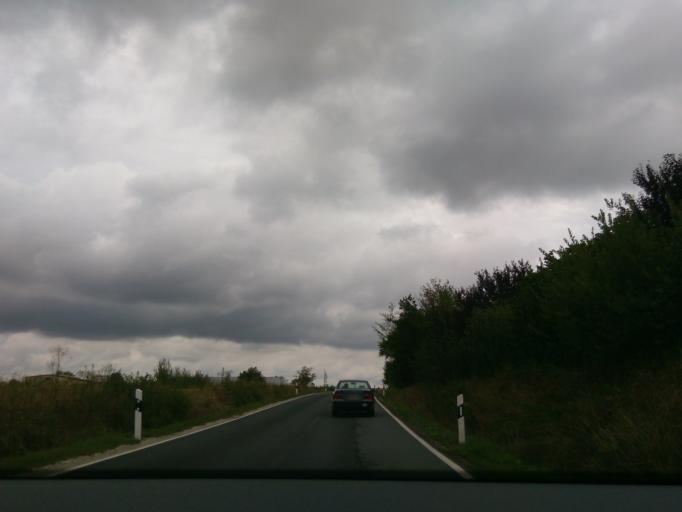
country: DE
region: Bavaria
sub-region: Regierungsbezirk Mittelfranken
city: Hochstadt an der Aisch
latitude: 49.6906
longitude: 10.8038
